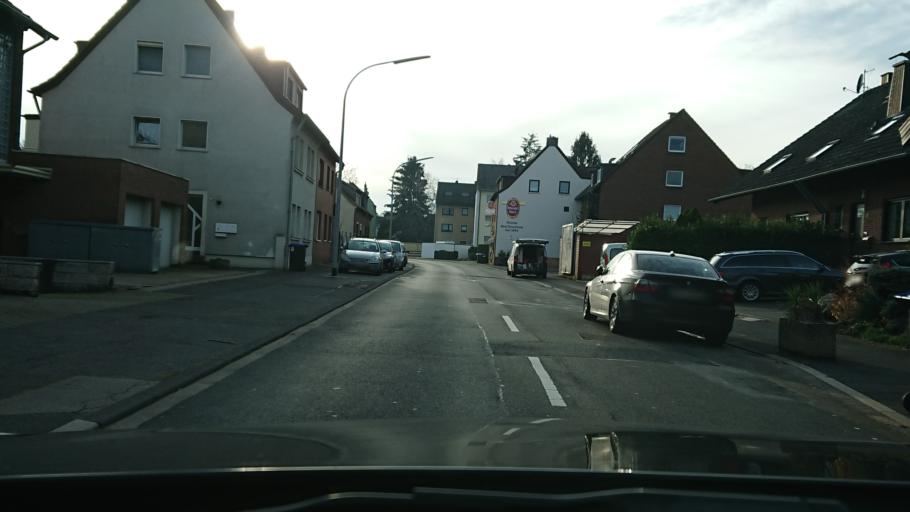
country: DE
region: North Rhine-Westphalia
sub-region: Regierungsbezirk Koln
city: Frechen
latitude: 50.8931
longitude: 6.8399
